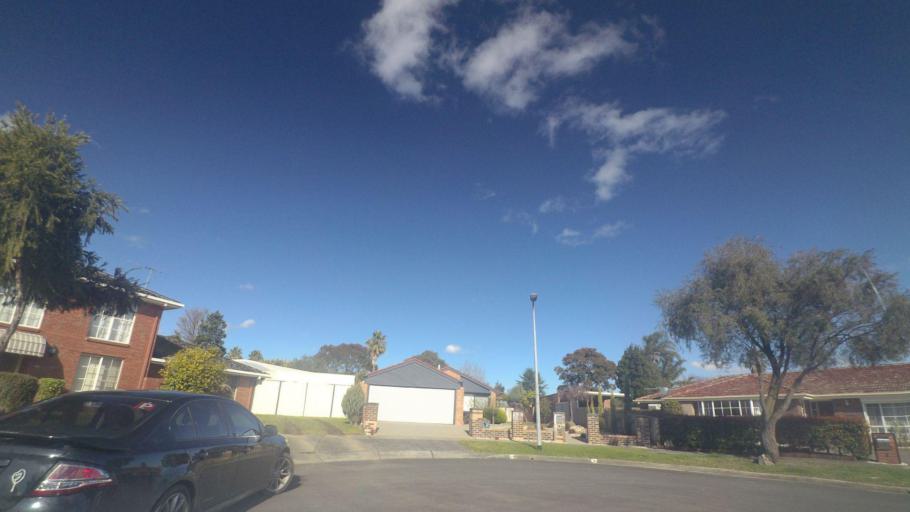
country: AU
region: Victoria
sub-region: Knox
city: Knoxfield
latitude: -37.9140
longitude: 145.2553
